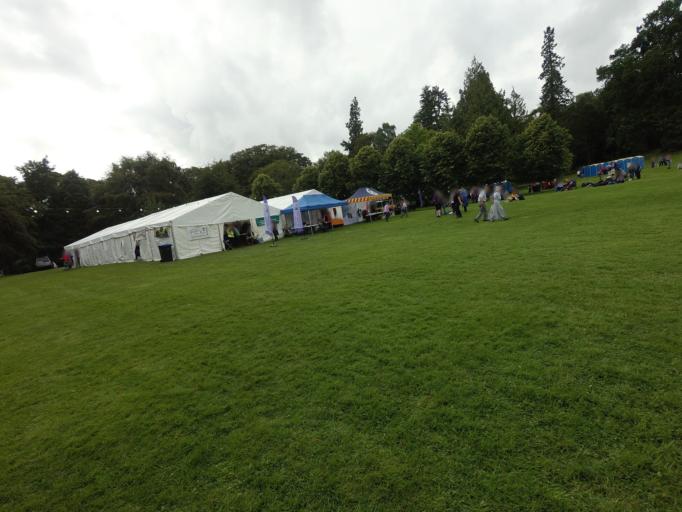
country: GB
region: Scotland
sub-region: Aberdeenshire
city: Banchory
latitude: 57.0608
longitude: -2.4402
